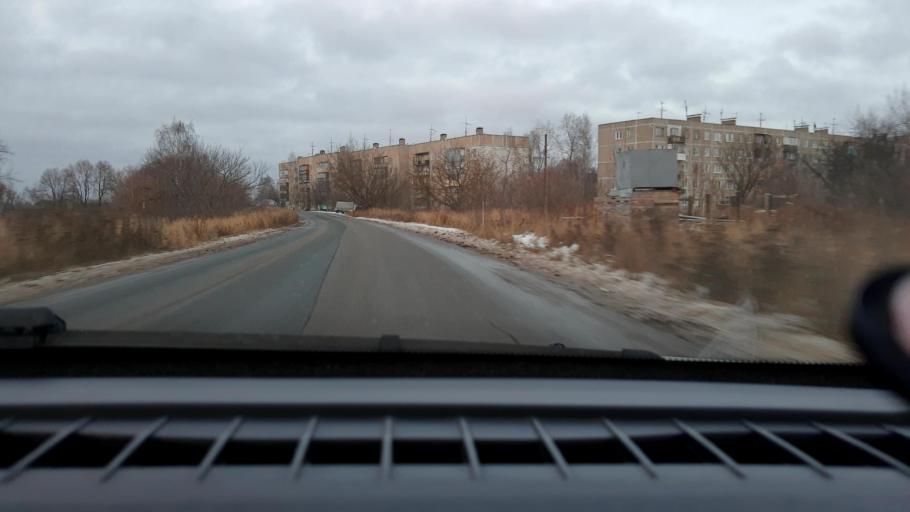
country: RU
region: Nizjnij Novgorod
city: Gorbatovka
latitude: 56.2427
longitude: 43.7455
